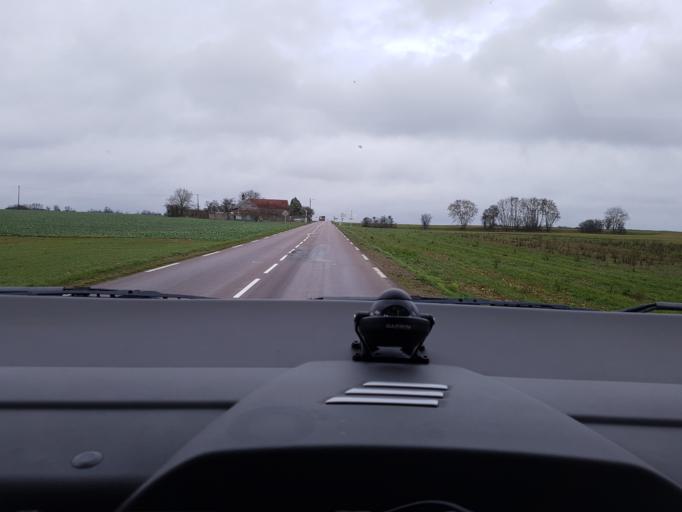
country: FR
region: Picardie
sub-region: Departement de l'Oise
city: Songeons
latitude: 49.5126
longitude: 1.8161
